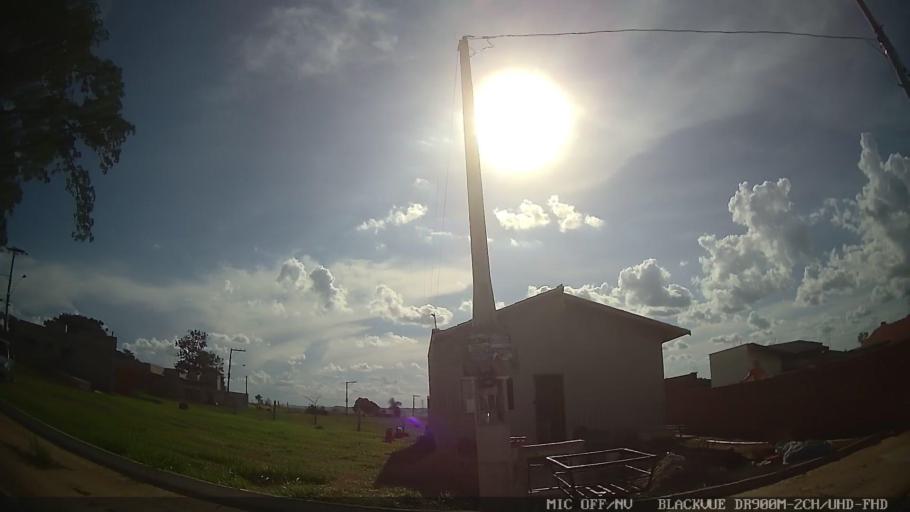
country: BR
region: Sao Paulo
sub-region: Laranjal Paulista
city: Laranjal Paulista
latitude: -23.0858
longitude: -47.7943
